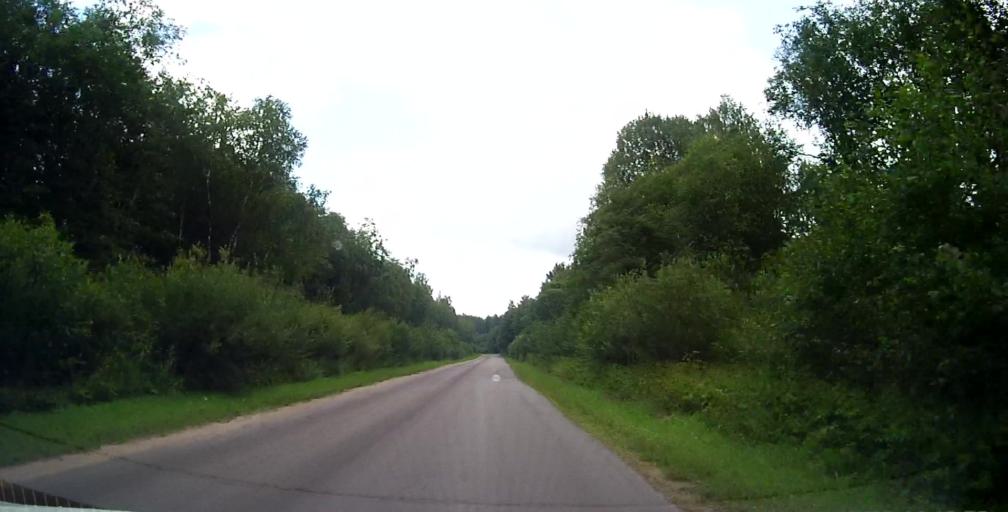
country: RU
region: Smolensk
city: Demidov
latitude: 55.4734
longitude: 31.6316
